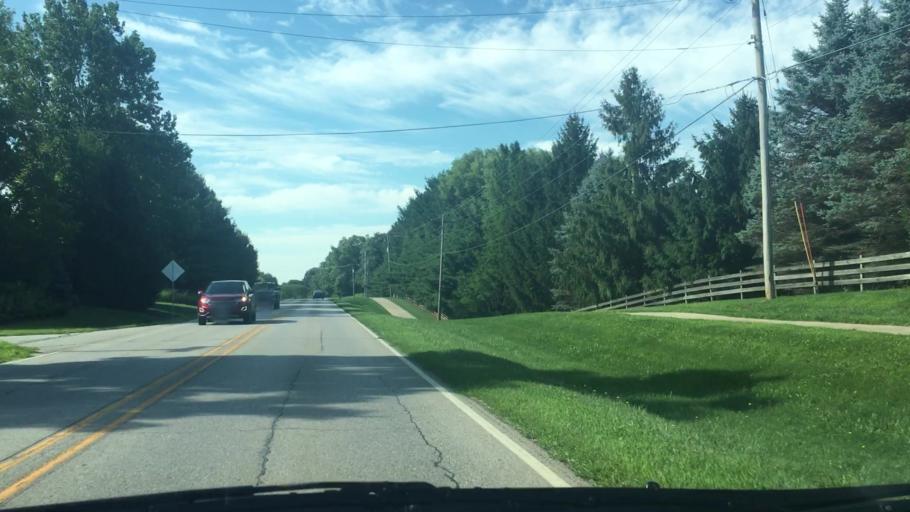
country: US
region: Iowa
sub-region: Johnson County
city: Coralville
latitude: 41.7132
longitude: -91.5510
